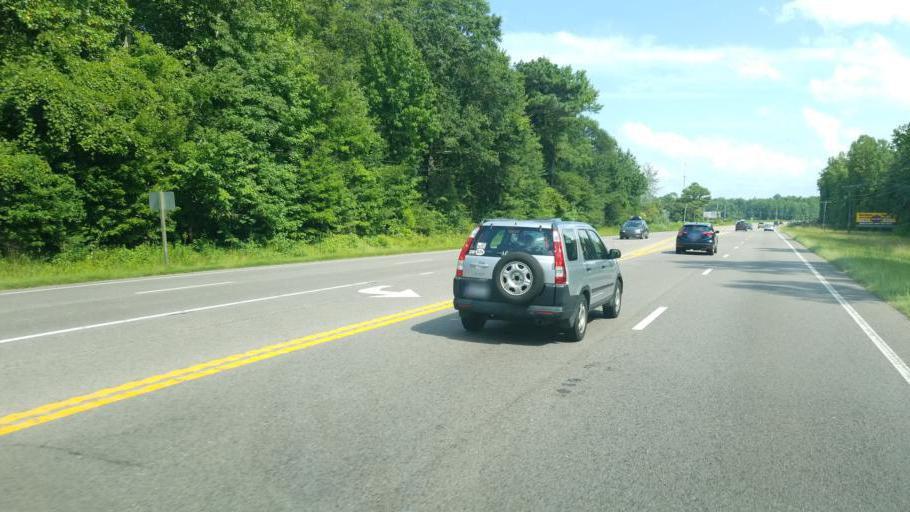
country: US
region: North Carolina
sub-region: Currituck County
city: Currituck
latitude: 36.3041
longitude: -75.9294
